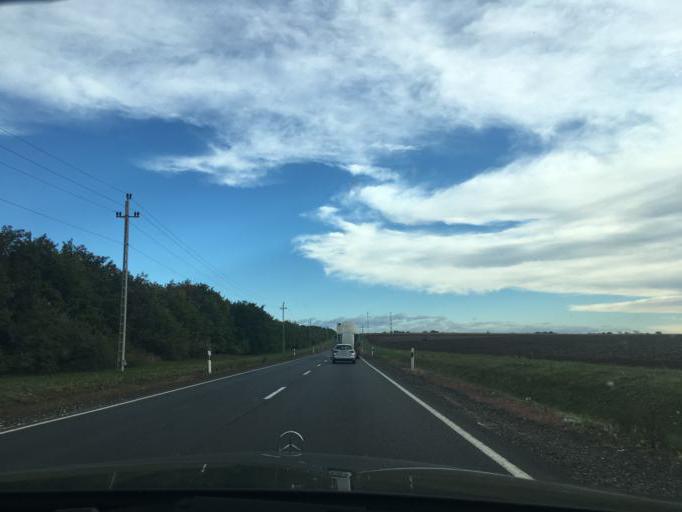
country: HU
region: Borsod-Abauj-Zemplen
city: Arnot
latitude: 48.1433
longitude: 20.8879
